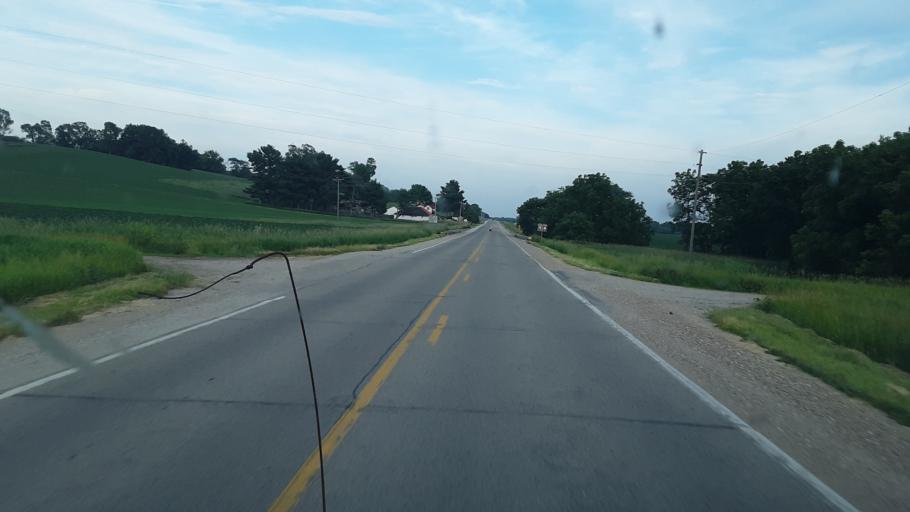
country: US
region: Iowa
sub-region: Benton County
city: Belle Plaine
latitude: 41.9119
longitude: -92.3469
